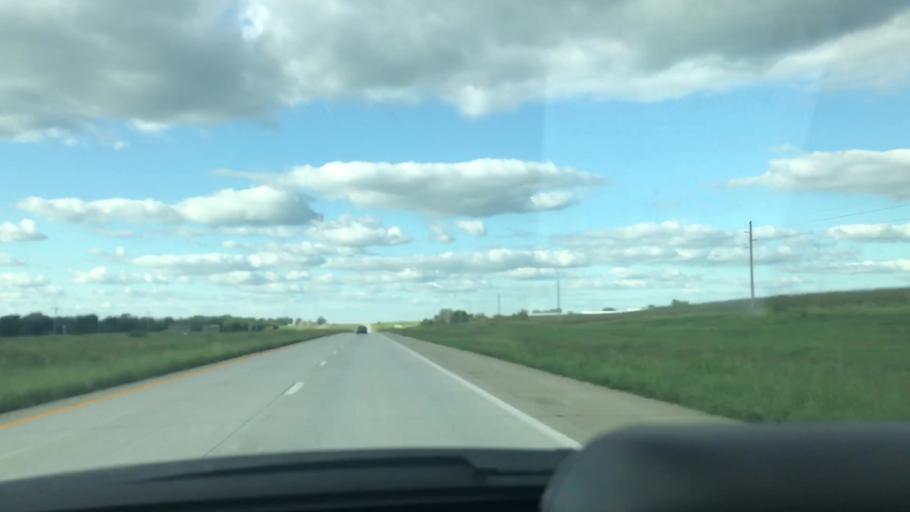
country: US
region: Missouri
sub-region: Benton County
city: Cole Camp
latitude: 38.4899
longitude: -93.2737
